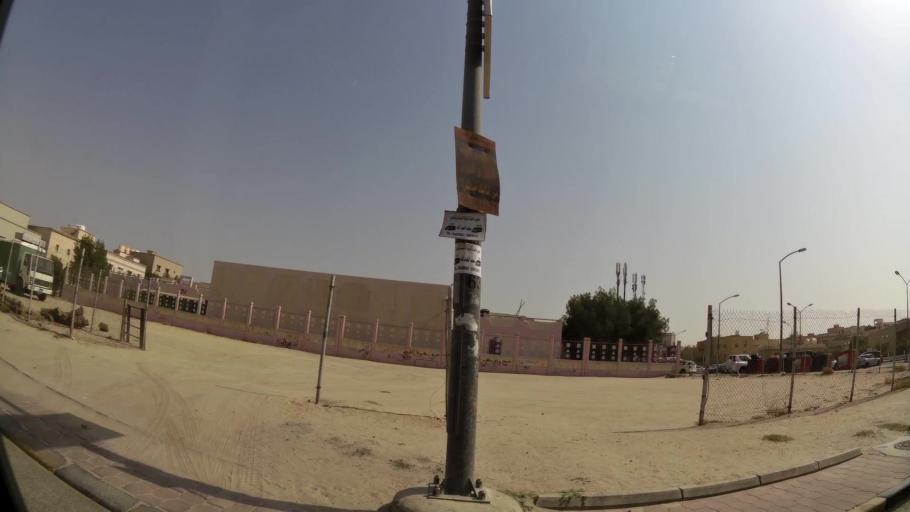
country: KW
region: Muhafazat al Jahra'
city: Al Jahra'
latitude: 29.3066
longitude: 47.6876
